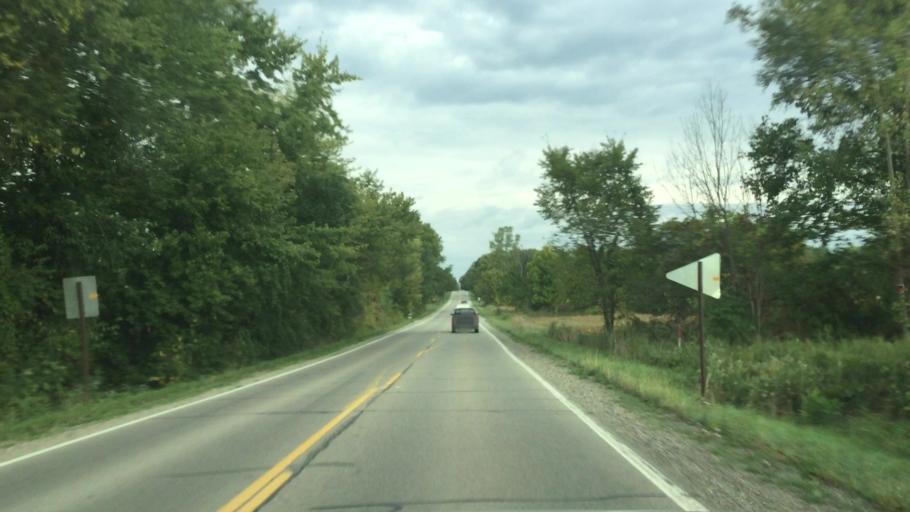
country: US
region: Michigan
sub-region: Livingston County
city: Howell
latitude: 42.6486
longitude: -83.8761
